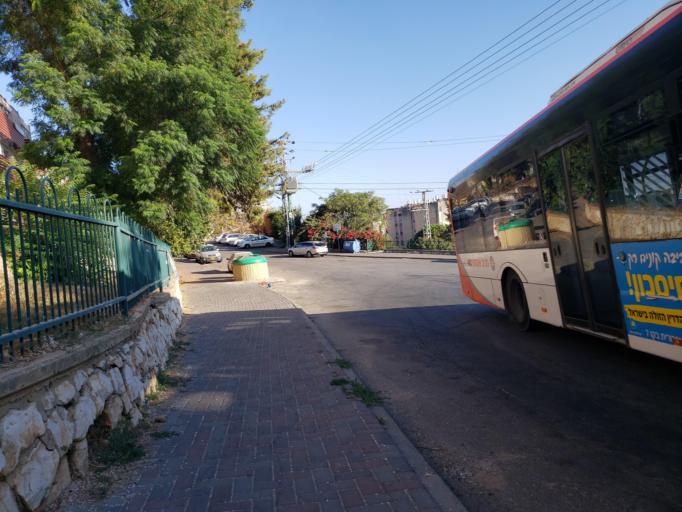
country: IL
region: Northern District
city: Safed
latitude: 32.9584
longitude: 35.4930
